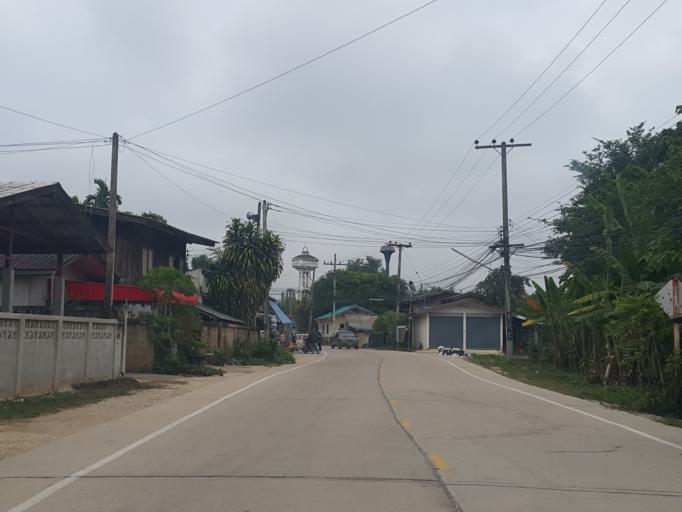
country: TH
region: Lampang
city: Lampang
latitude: 18.3188
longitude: 99.4912
